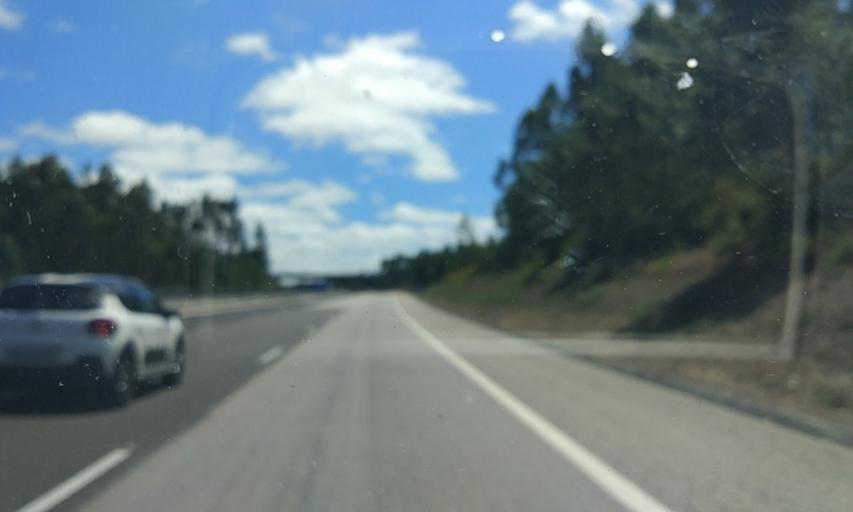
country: PT
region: Leiria
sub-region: Pombal
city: Lourical
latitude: 39.9995
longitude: -8.7989
